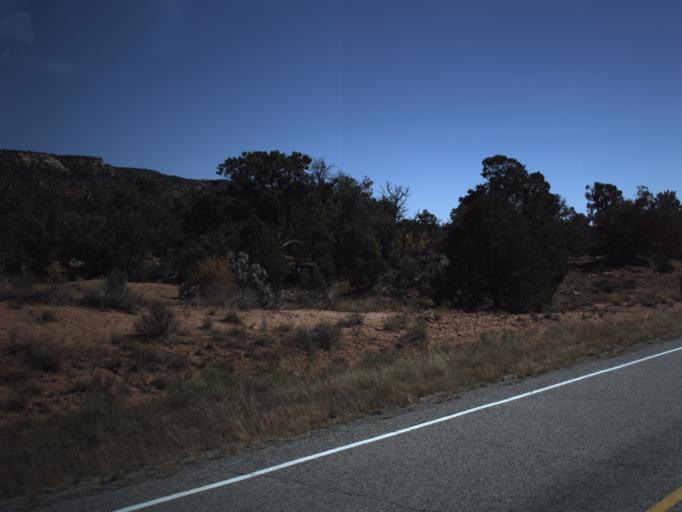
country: US
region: Utah
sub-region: San Juan County
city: Blanding
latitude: 37.5706
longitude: -109.8738
